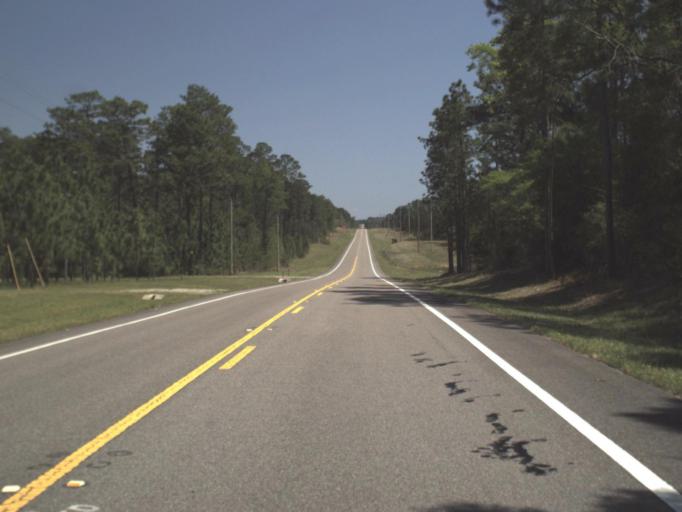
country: US
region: Florida
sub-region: Santa Rosa County
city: Point Baker
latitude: 30.8916
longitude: -86.9794
